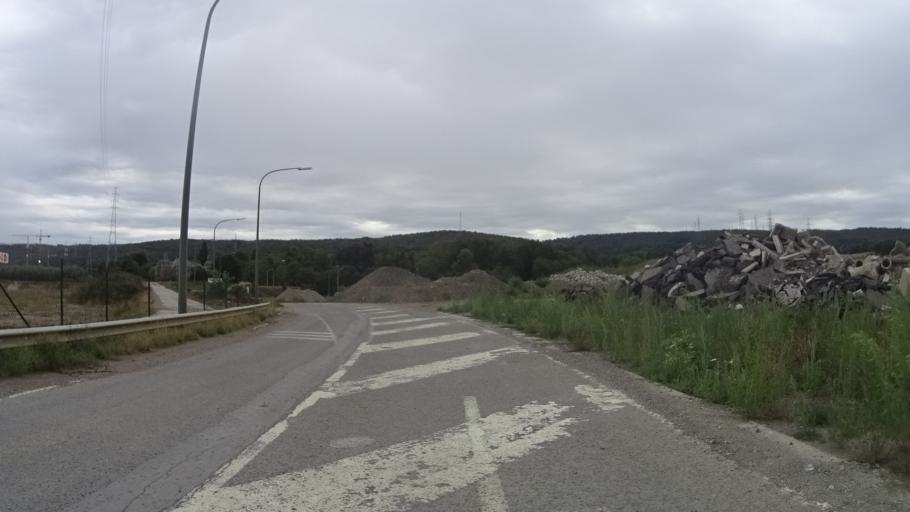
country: BE
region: Wallonia
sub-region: Province de Liege
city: Amay
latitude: 50.5339
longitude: 5.2834
